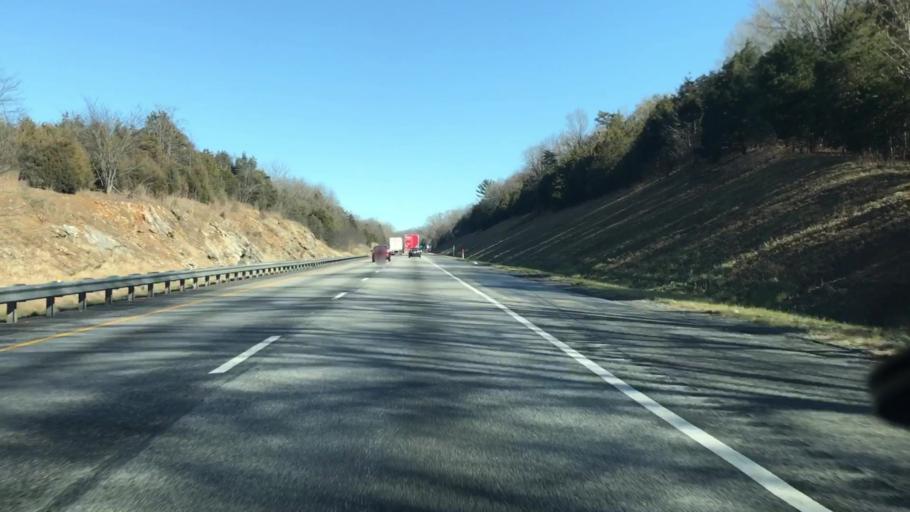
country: US
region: Virginia
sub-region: Rockbridge County
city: East Lexington
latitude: 37.8162
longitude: -79.3821
